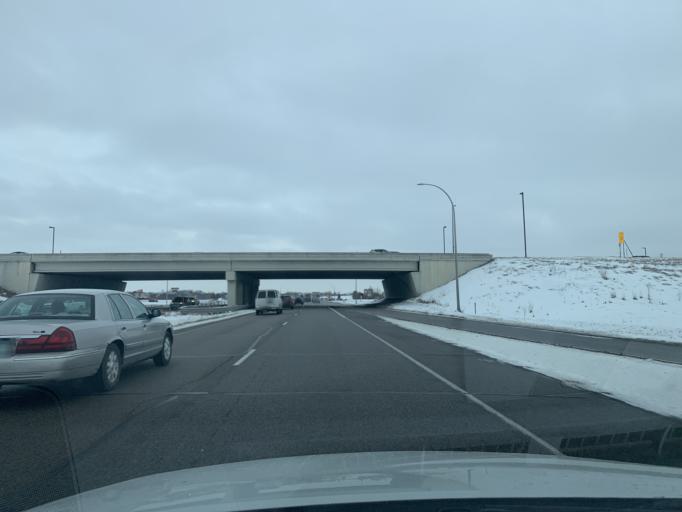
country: US
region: Minnesota
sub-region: Anoka County
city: Anoka
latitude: 45.2043
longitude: -93.3590
